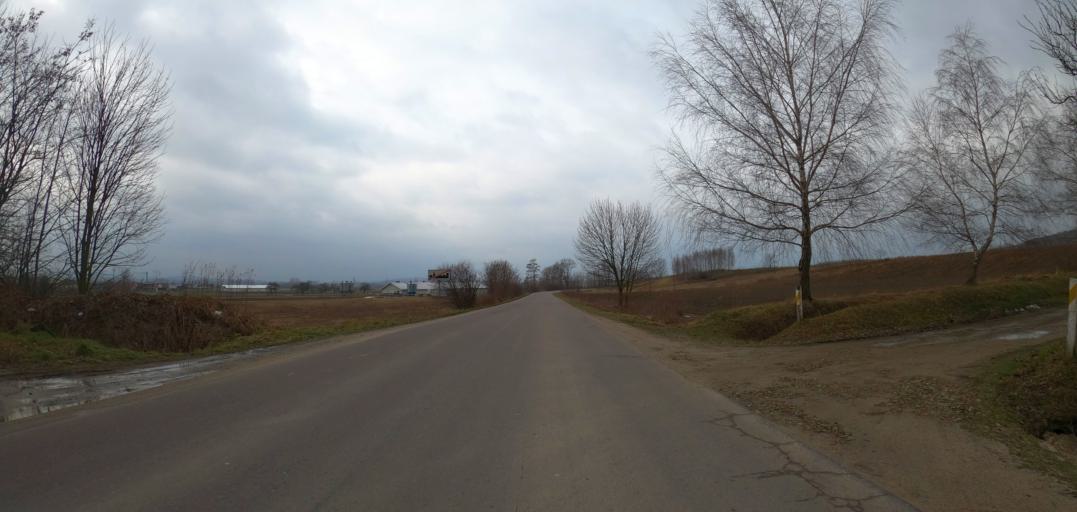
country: PL
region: Subcarpathian Voivodeship
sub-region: Powiat debicki
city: Pilzno
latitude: 49.9808
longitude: 21.3325
